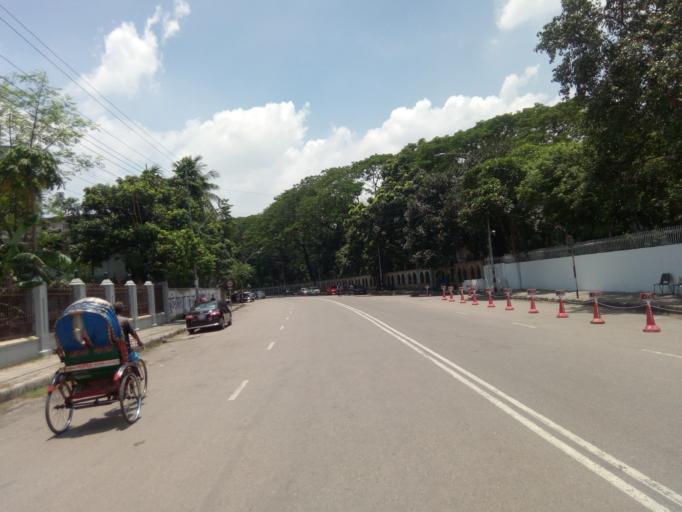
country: BD
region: Dhaka
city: Azimpur
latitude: 23.7308
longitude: 90.3919
